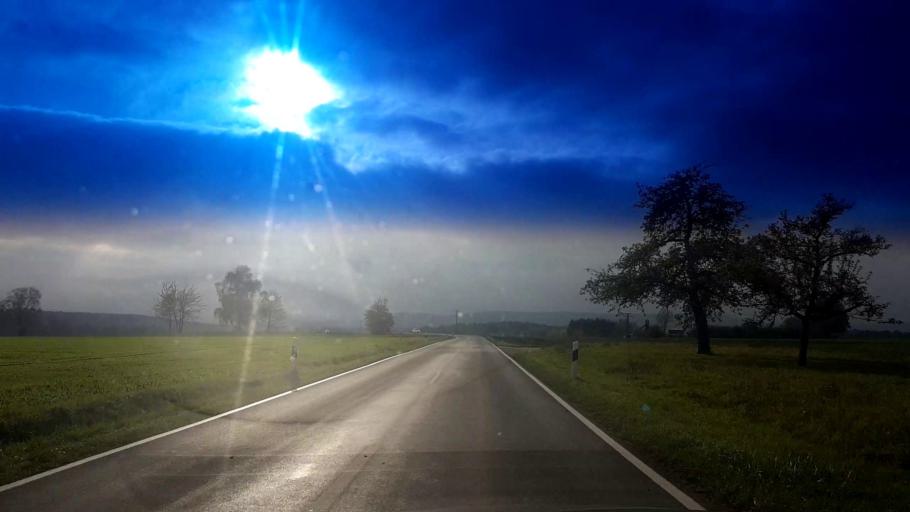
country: DE
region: Bavaria
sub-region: Upper Franconia
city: Zapfendorf
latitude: 49.9782
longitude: 10.9393
